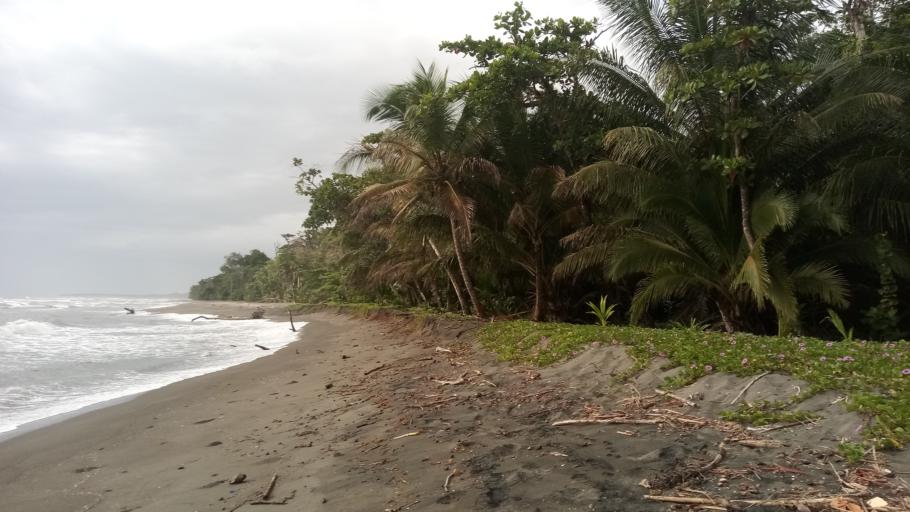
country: CR
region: Limon
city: Sixaola
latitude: 9.6134
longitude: -82.6187
